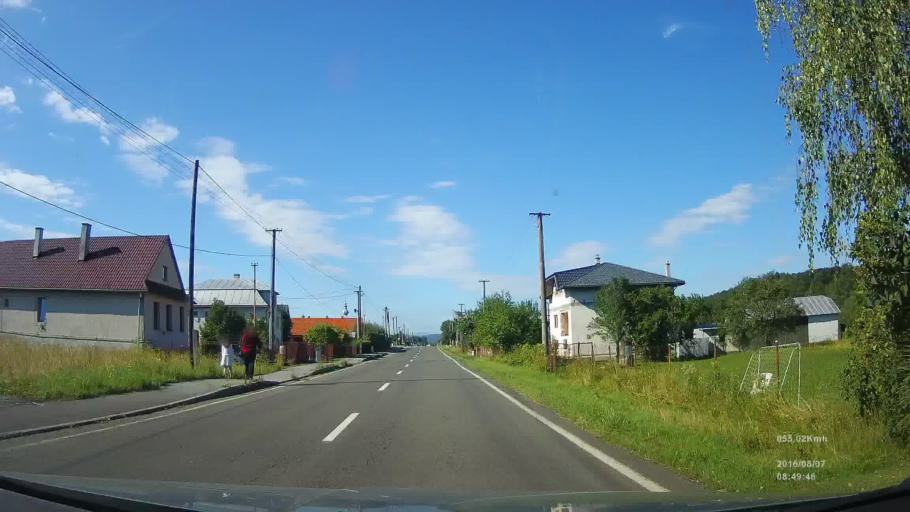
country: SK
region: Presovsky
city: Stropkov
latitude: 49.2506
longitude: 21.6866
